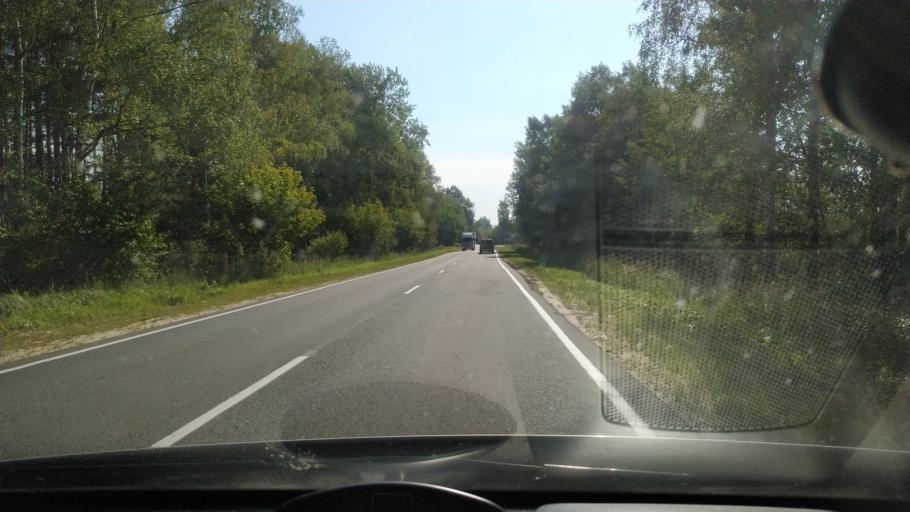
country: RU
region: Rjazan
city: Spas-Klepiki
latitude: 55.2208
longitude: 40.0865
